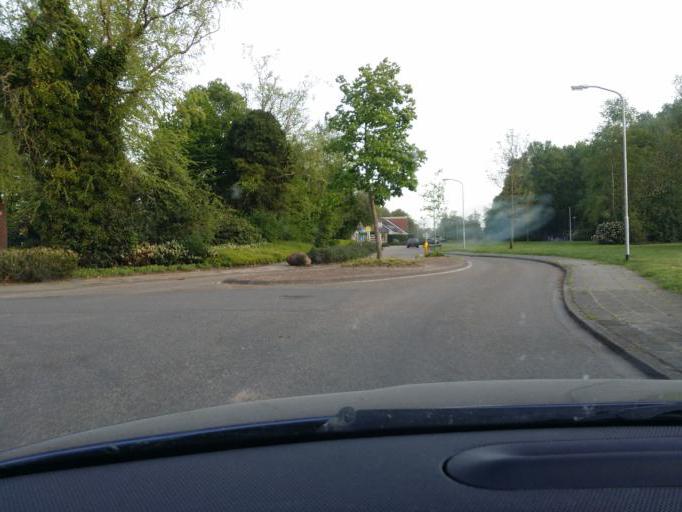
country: NL
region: Groningen
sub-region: Gemeente Grootegast
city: Grootegast
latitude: 53.2112
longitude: 6.2744
